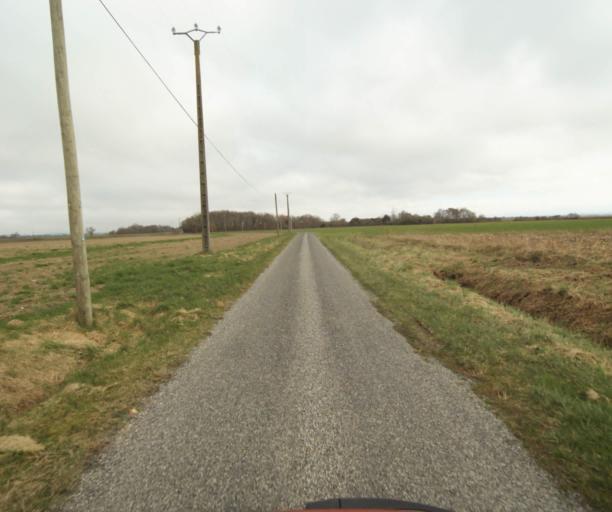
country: FR
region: Midi-Pyrenees
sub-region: Departement de l'Ariege
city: Mazeres
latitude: 43.1830
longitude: 1.6723
